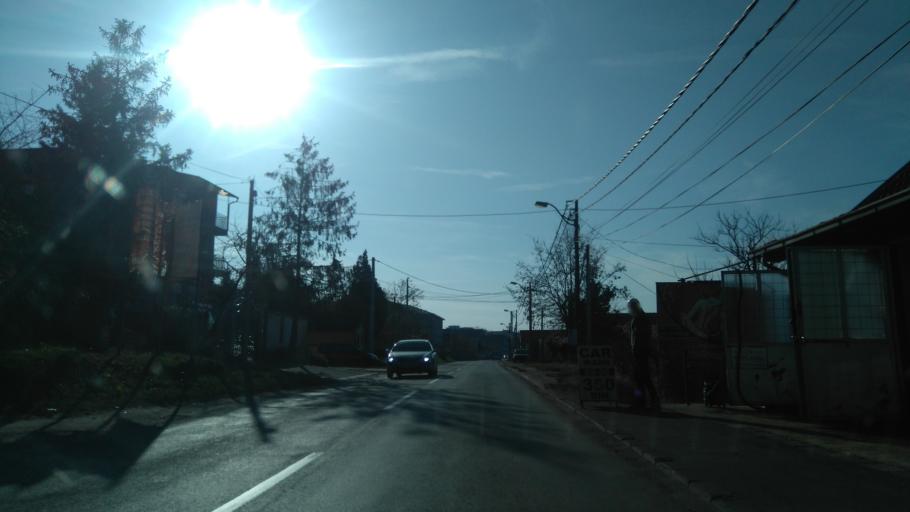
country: RS
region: Central Serbia
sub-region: Belgrade
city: Rakovica
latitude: 44.7392
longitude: 20.3874
